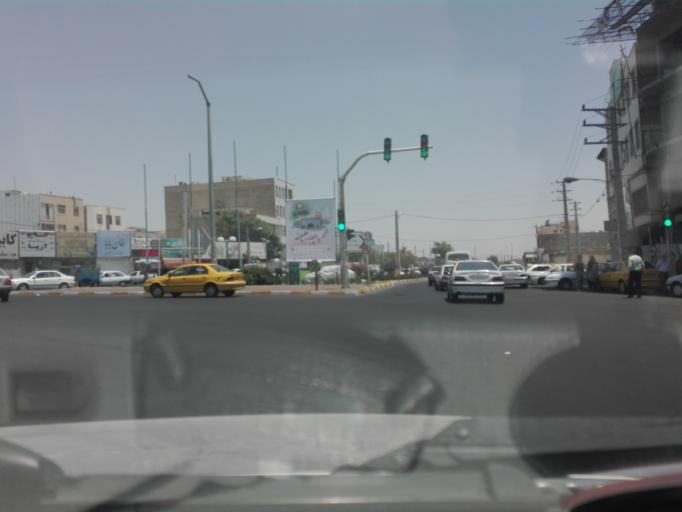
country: IR
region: Tehran
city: Malard
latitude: 35.7097
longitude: 50.9844
